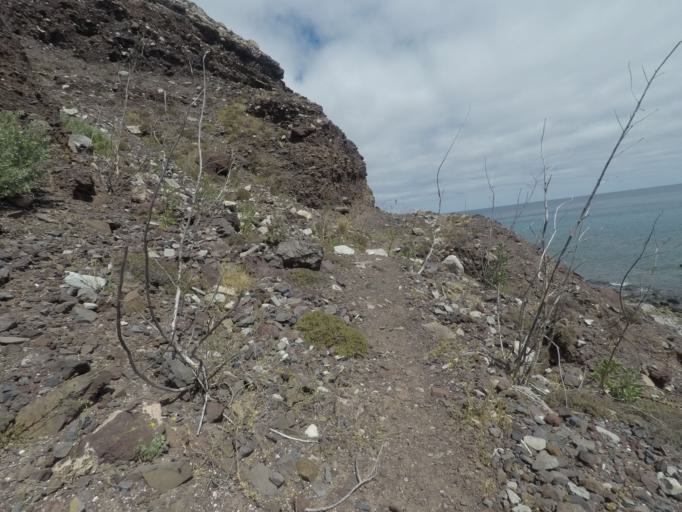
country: PT
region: Madeira
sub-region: Porto Santo
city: Vila de Porto Santo
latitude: 33.0605
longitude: -16.3005
